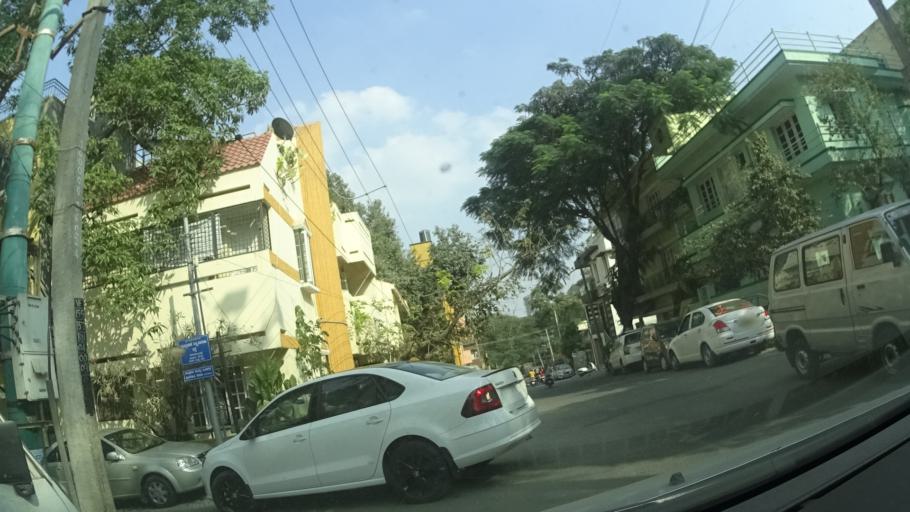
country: IN
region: Karnataka
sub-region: Bangalore Urban
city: Bangalore
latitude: 12.9495
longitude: 77.5603
